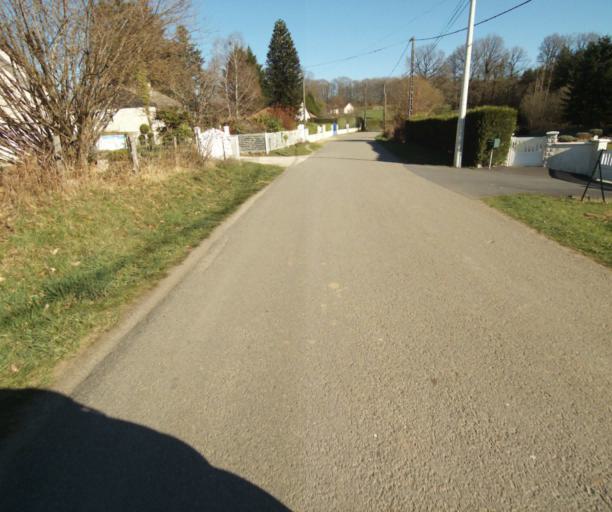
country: FR
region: Limousin
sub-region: Departement de la Correze
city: Seilhac
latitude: 45.3859
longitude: 1.7159
